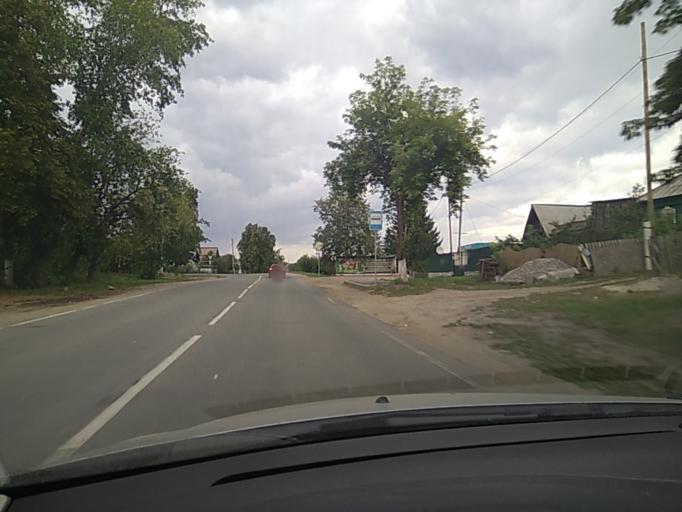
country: RU
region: Chelyabinsk
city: Kyshtym
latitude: 55.7089
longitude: 60.5190
